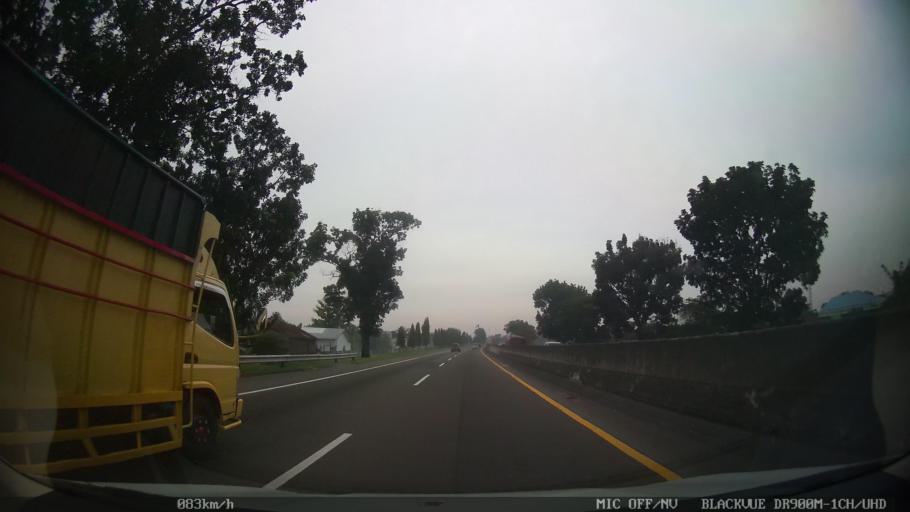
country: ID
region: North Sumatra
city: Medan
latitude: 3.5709
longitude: 98.7257
